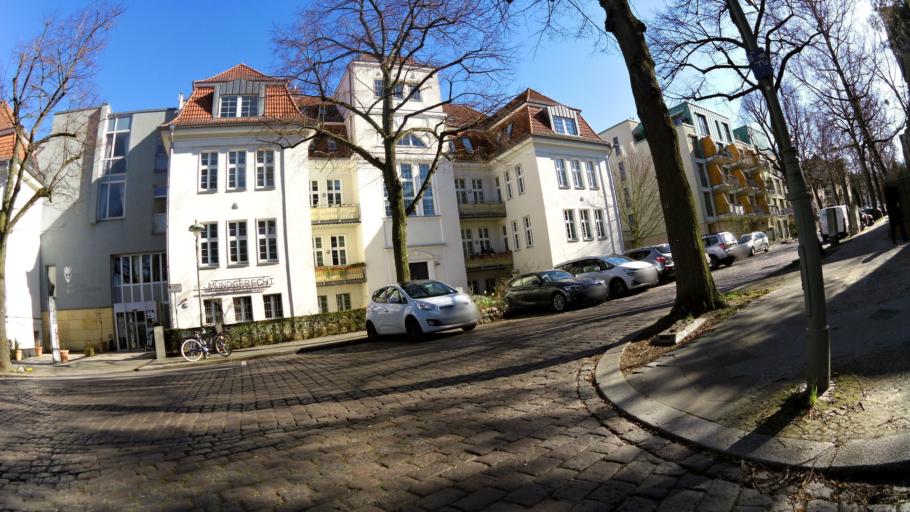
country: DE
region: Berlin
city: Friedenau
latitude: 52.4614
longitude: 13.3114
